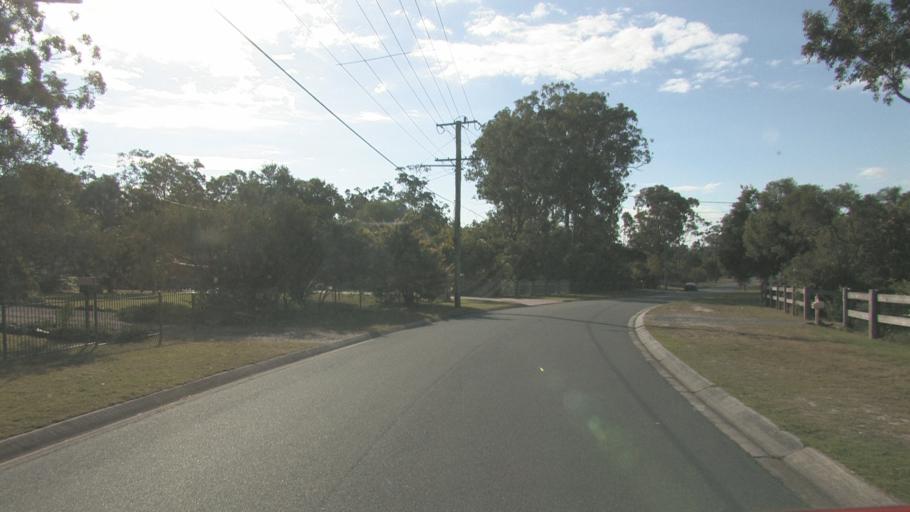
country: AU
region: Queensland
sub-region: Logan
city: Windaroo
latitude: -27.7580
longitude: 153.1916
